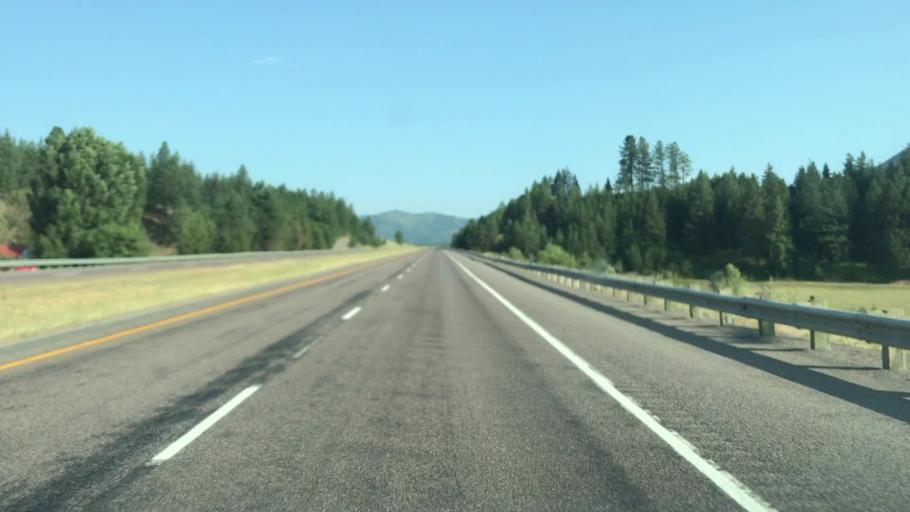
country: US
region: Montana
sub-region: Mineral County
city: Superior
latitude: 47.0540
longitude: -114.7597
